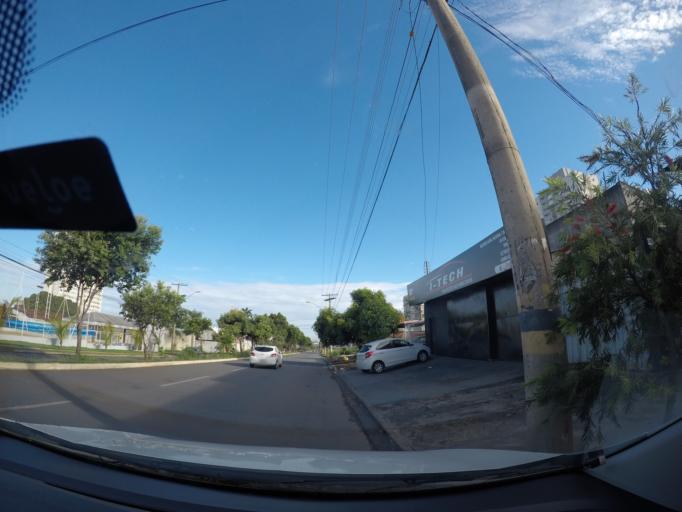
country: BR
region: Goias
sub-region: Goiania
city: Goiania
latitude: -16.7413
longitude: -49.2839
